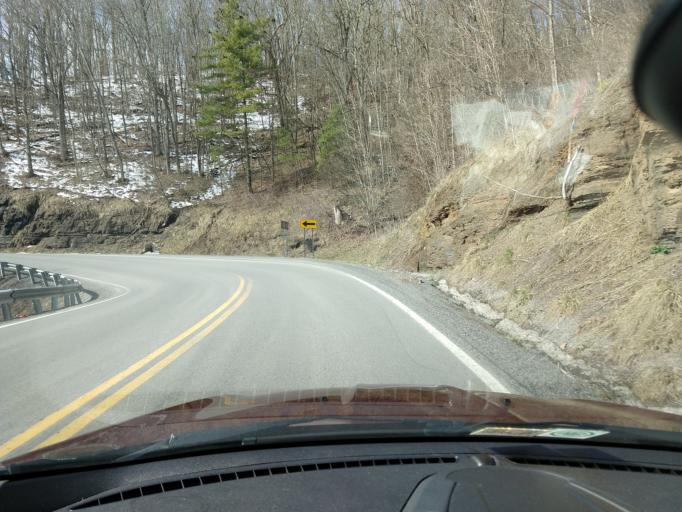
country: US
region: West Virginia
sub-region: Pocahontas County
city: Marlinton
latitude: 38.1150
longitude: -80.2611
